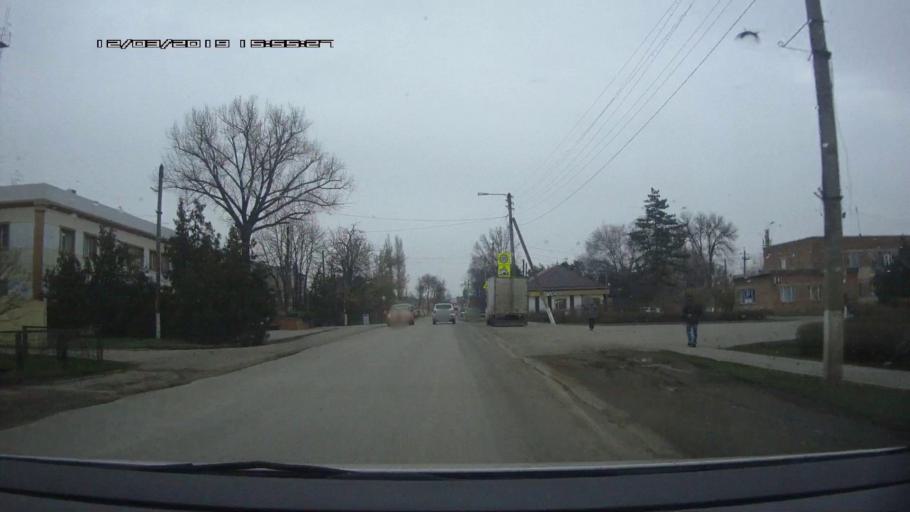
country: RU
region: Rostov
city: Novobataysk
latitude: 46.8967
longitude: 39.7798
